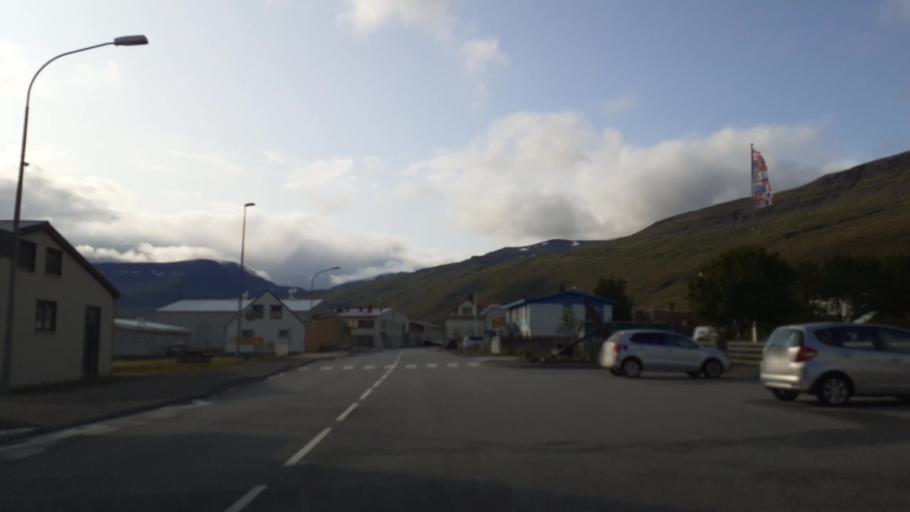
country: IS
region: East
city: Eskifjoerdur
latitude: 65.0709
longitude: -14.0135
